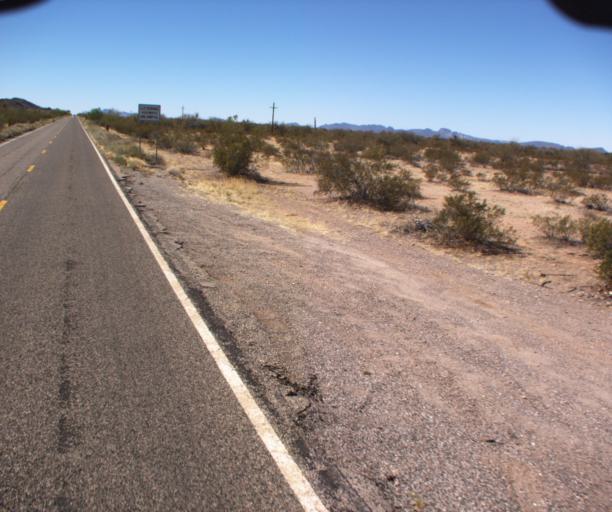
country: US
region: Arizona
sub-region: Pima County
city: Ajo
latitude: 32.2506
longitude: -112.7457
